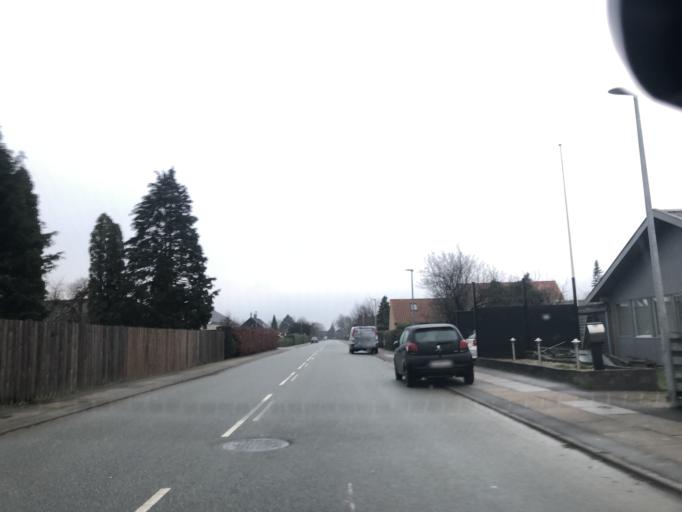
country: DK
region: Capital Region
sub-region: Tarnby Kommune
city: Tarnby
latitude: 55.6377
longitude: 12.5960
